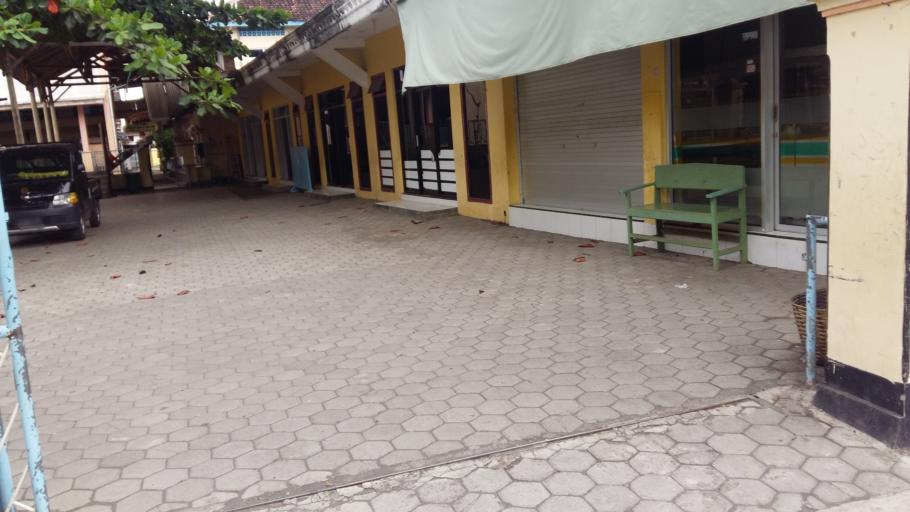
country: ID
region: East Java
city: Krajan
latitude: -8.3081
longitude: 114.2921
